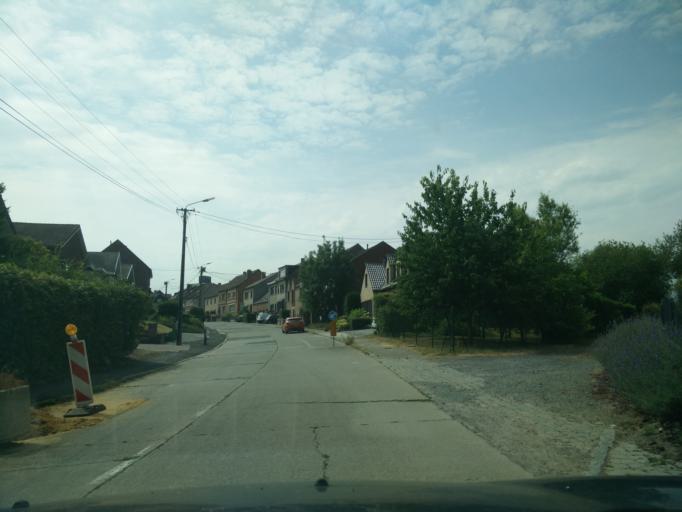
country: BE
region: Wallonia
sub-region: Province du Brabant Wallon
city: Tubize
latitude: 50.6938
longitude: 4.2211
